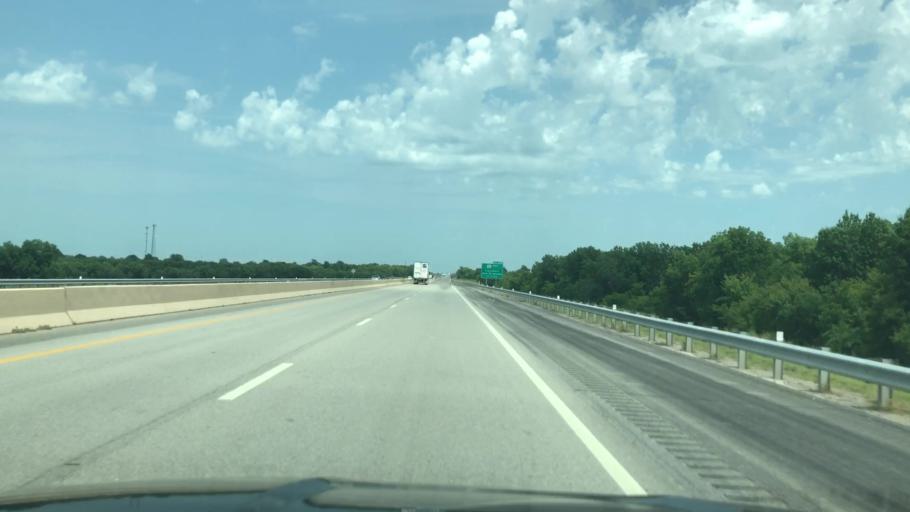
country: US
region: Oklahoma
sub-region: Rogers County
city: Verdigris
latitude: 36.2133
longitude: -95.6956
